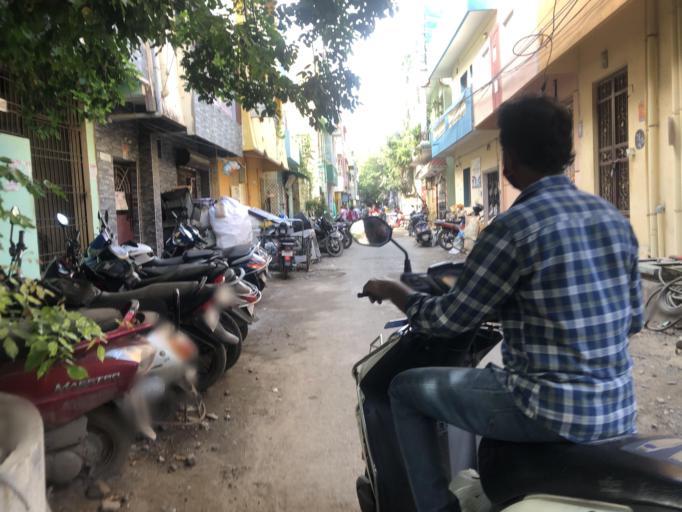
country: IN
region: Tamil Nadu
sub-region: Chennai
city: Gandhi Nagar
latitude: 13.0347
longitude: 80.2583
